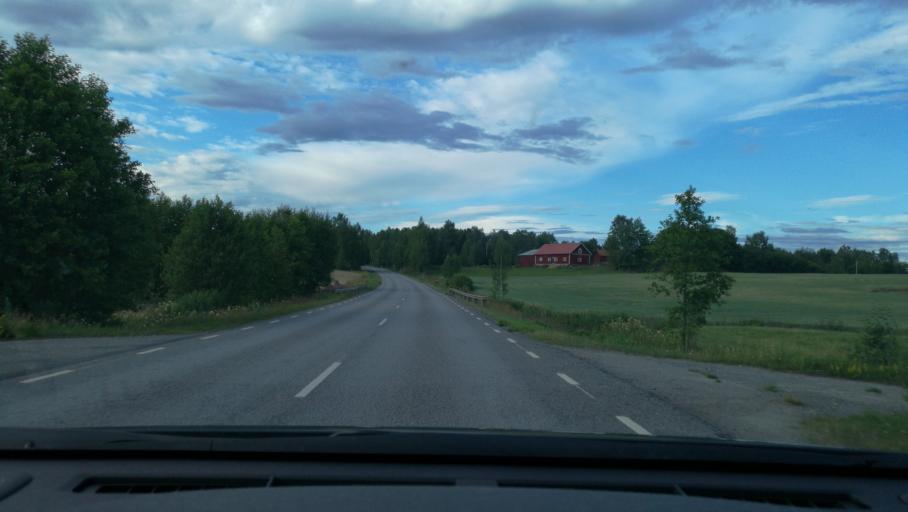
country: SE
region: OEstergoetland
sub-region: Norrkopings Kommun
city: Svartinge
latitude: 58.7150
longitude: 15.9387
